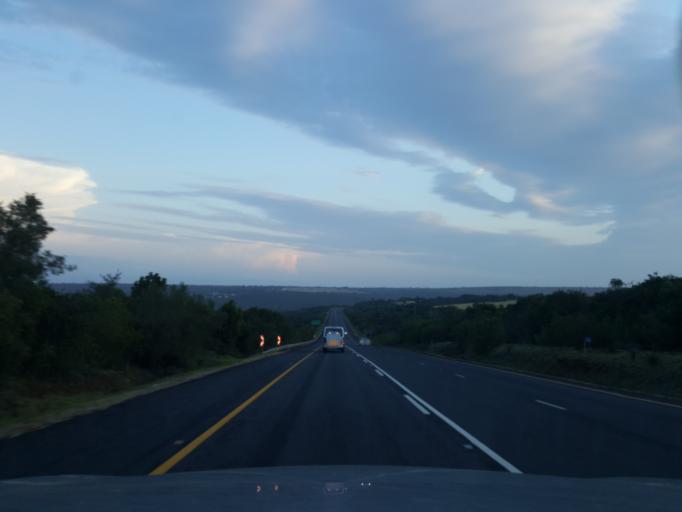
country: ZA
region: Eastern Cape
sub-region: Cacadu District Municipality
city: Grahamstown
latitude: -33.3860
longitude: 26.4405
